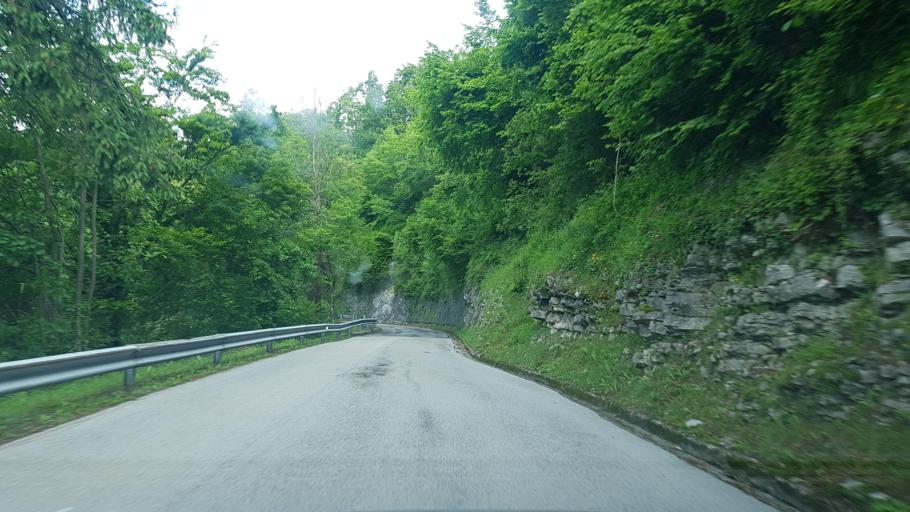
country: IT
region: Friuli Venezia Giulia
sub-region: Provincia di Udine
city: Arta Terme
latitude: 46.4680
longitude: 13.0149
